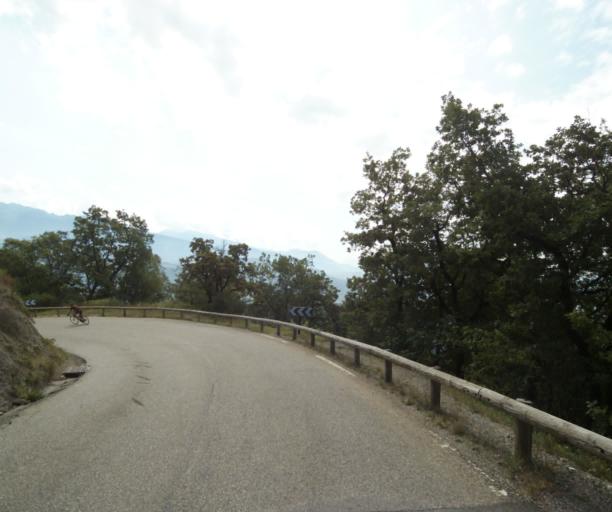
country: FR
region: Rhone-Alpes
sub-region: Departement de l'Isere
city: Corenc
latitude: 45.2295
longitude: 5.7547
